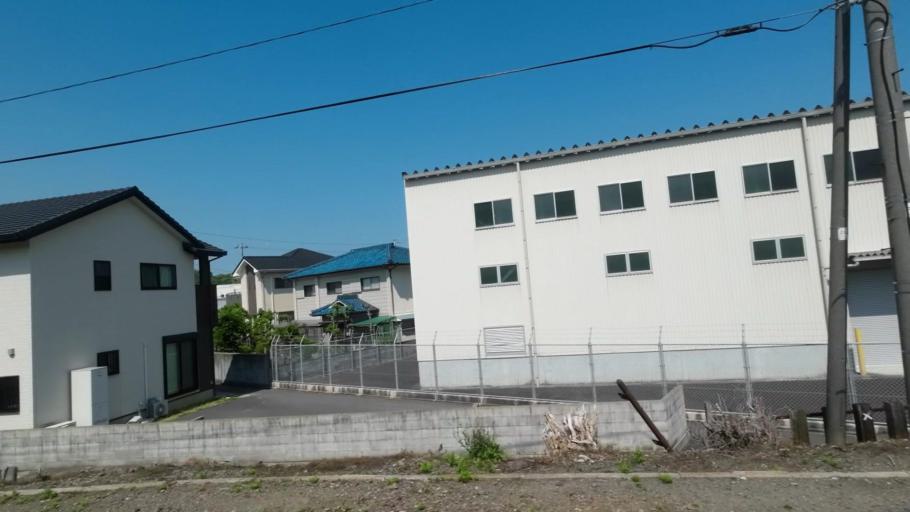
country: JP
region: Ehime
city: Kawanoecho
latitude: 34.0158
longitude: 133.5763
